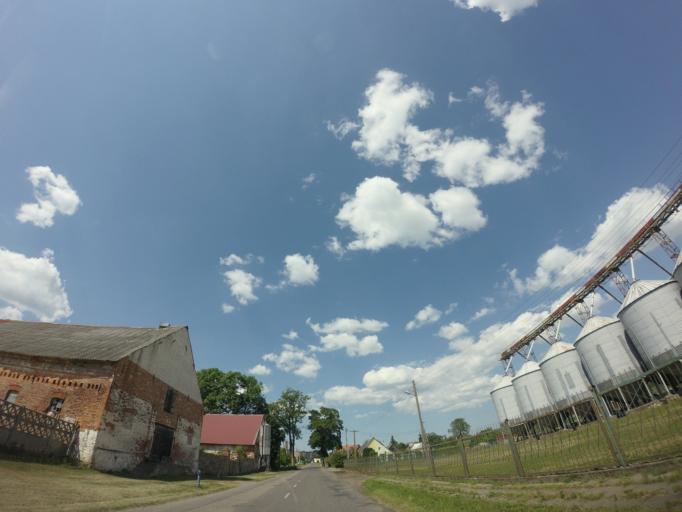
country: PL
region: West Pomeranian Voivodeship
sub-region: Powiat choszczenski
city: Pelczyce
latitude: 53.1158
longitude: 15.2527
